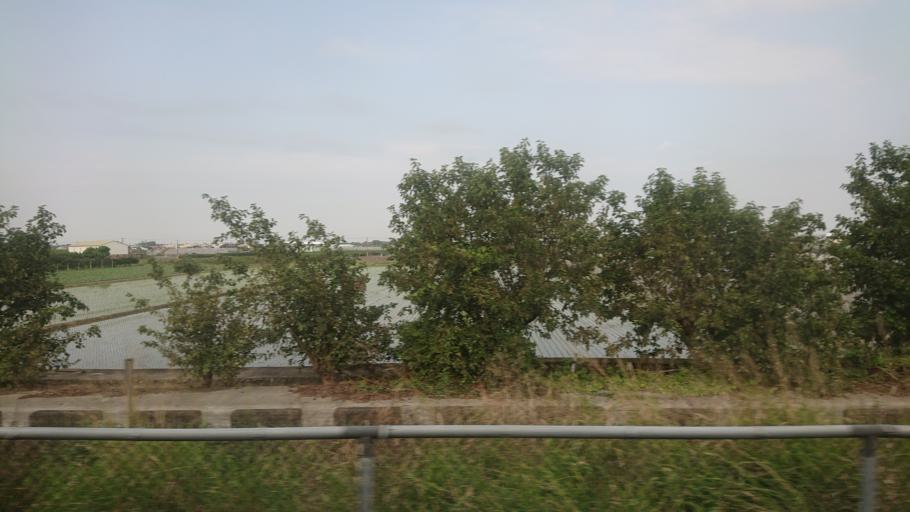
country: TW
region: Taiwan
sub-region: Yunlin
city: Douliu
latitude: 23.7336
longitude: 120.5817
